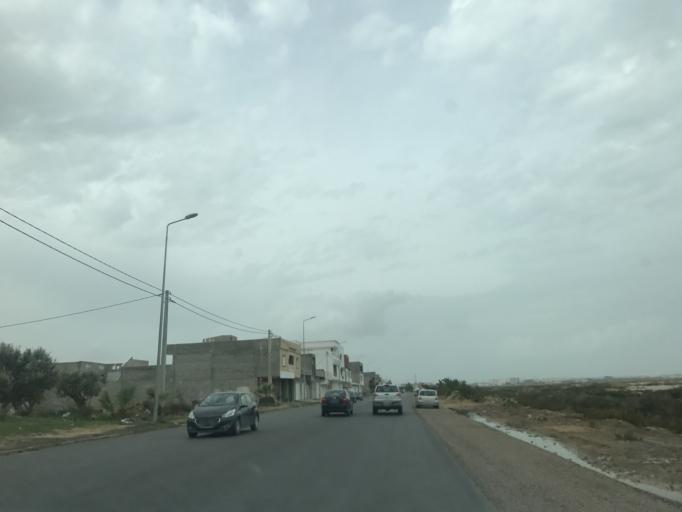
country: TN
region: Al Munastir
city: Banbalah
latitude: 35.7047
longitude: 10.8252
